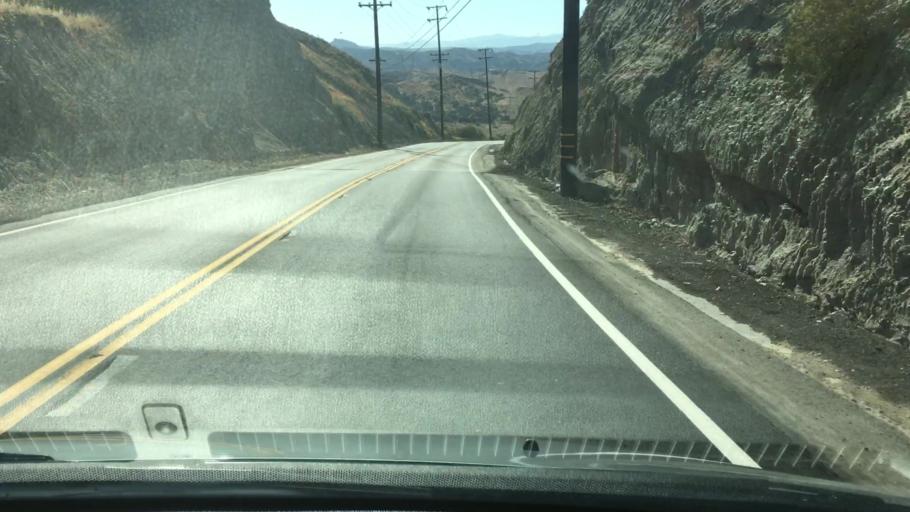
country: US
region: California
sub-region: Los Angeles County
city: Agua Dulce
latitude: 34.4709
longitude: -118.4319
